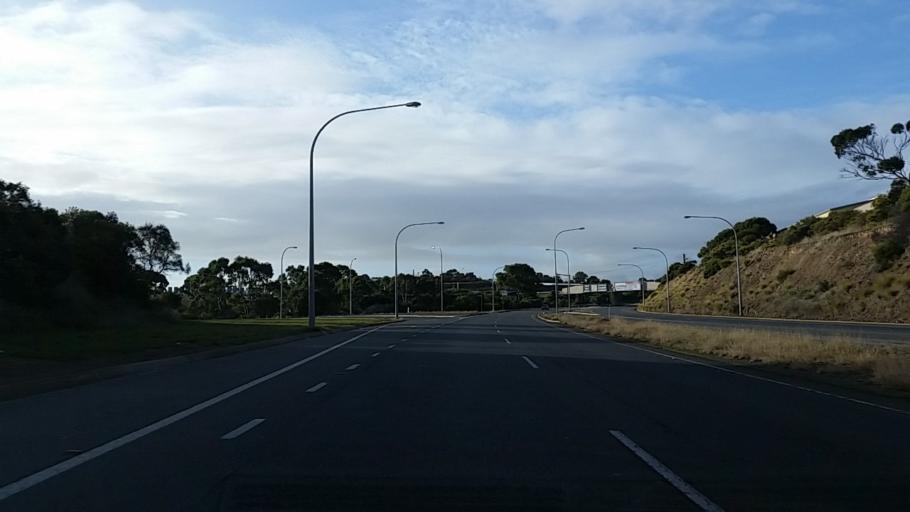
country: AU
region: South Australia
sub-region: Onkaparinga
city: Morphett Vale
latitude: -35.1142
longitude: 138.4913
